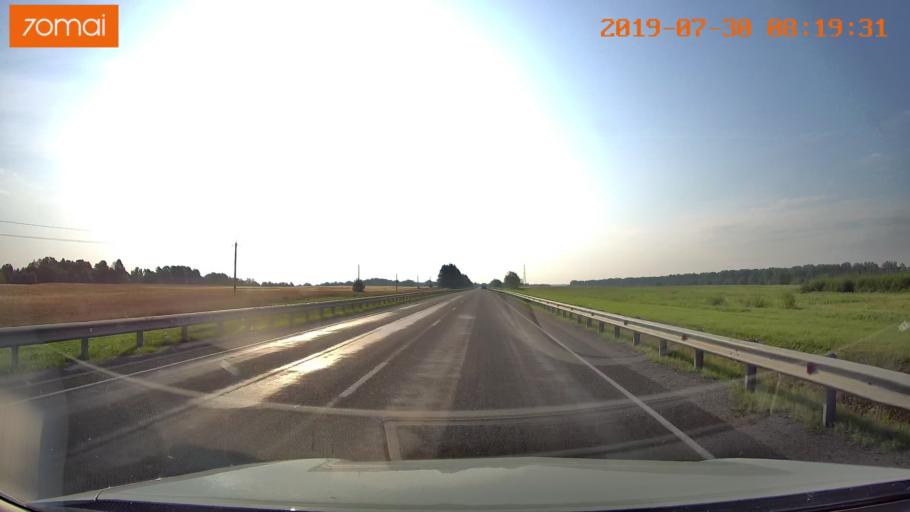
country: RU
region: Kaliningrad
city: Chernyakhovsk
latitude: 54.6281
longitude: 21.4937
